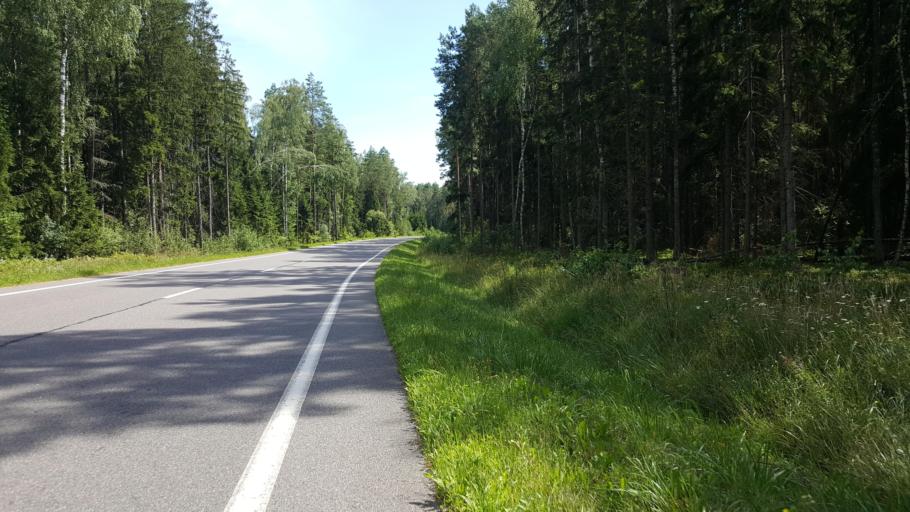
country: BY
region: Brest
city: Pruzhany
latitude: 52.5192
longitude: 24.1784
